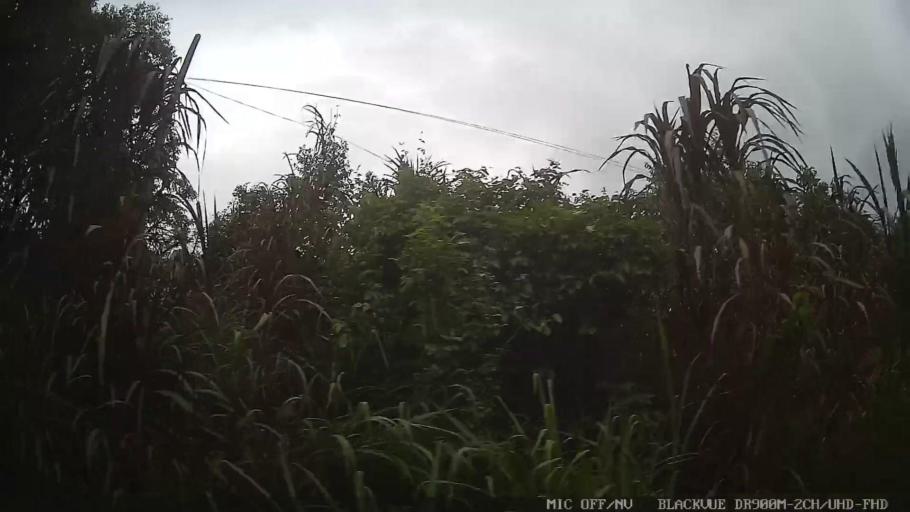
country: BR
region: Sao Paulo
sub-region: Aruja
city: Aruja
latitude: -23.4216
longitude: -46.2695
